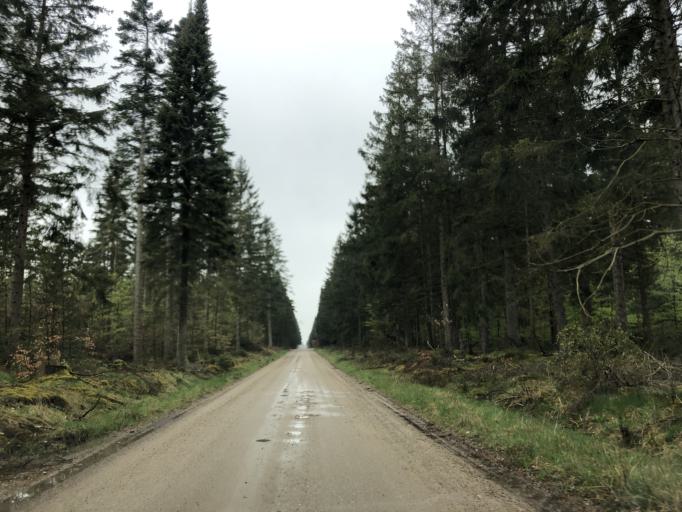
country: DK
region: Central Jutland
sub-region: Lemvig Kommune
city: Lemvig
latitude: 56.4880
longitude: 8.3548
